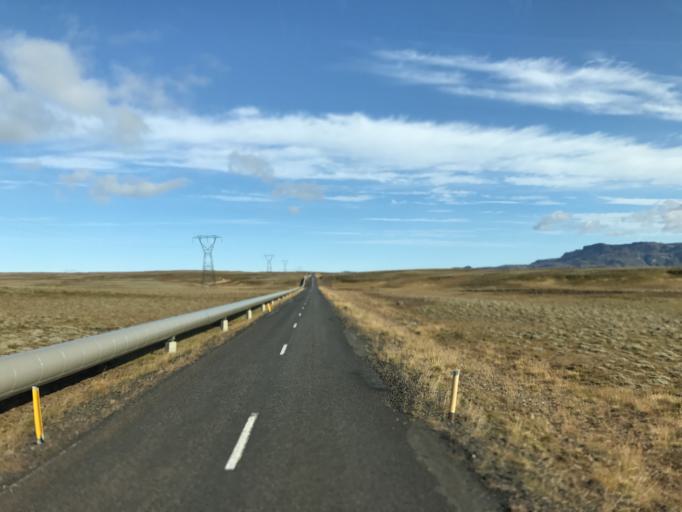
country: IS
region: Capital Region
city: Mosfellsbaer
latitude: 64.1146
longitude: -21.5058
